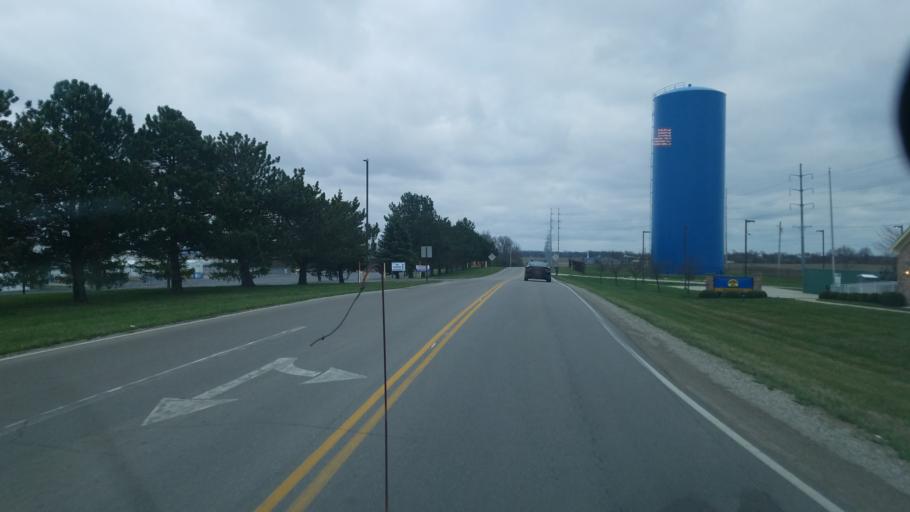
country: US
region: Ohio
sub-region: Fayette County
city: Washington Court House
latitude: 39.5270
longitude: -83.4711
